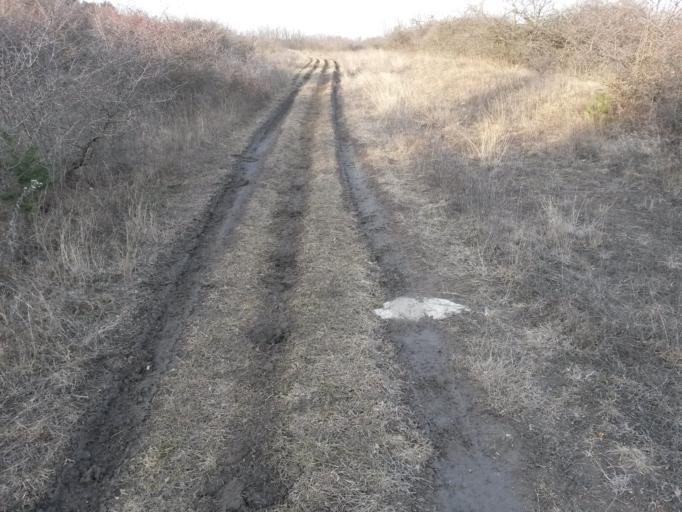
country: HU
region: Pest
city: Zsambek
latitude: 47.5820
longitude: 18.7197
